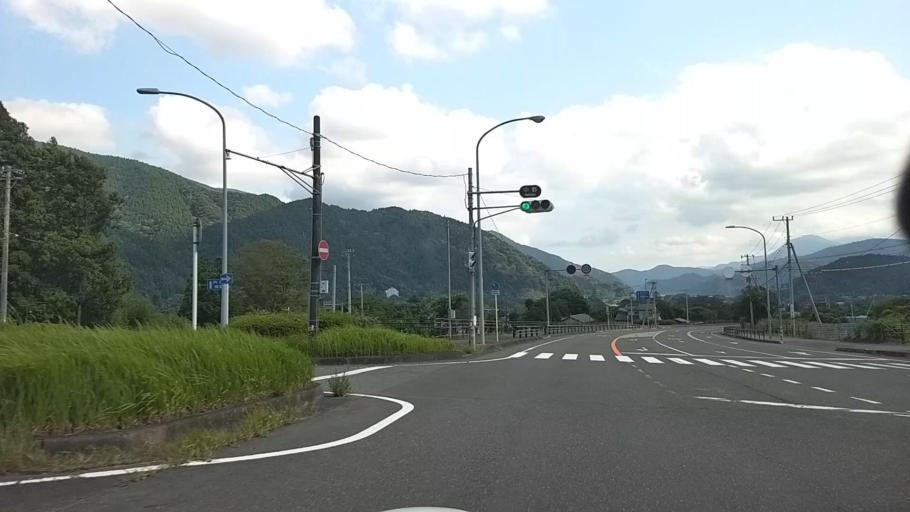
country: JP
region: Shizuoka
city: Fujinomiya
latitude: 35.3096
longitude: 138.4469
